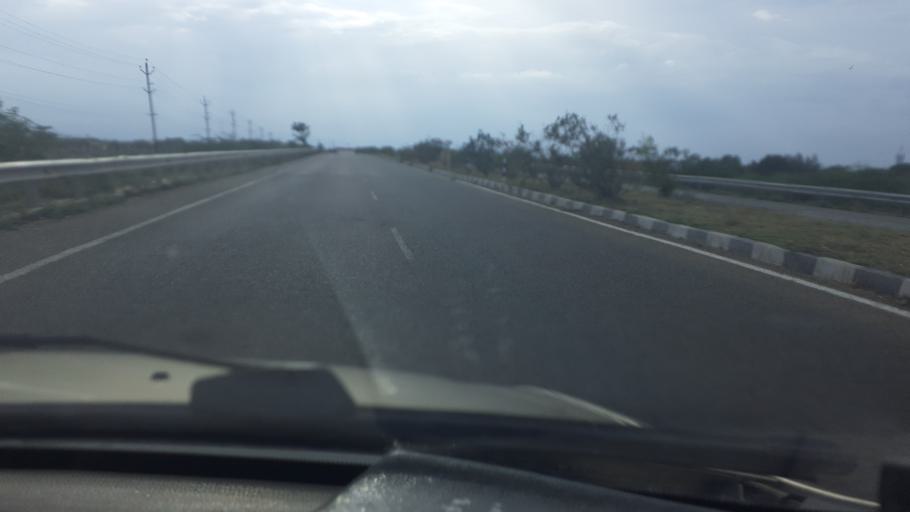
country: IN
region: Tamil Nadu
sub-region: Tirunelveli Kattabo
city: Tirunelveli
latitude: 8.6675
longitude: 77.7448
